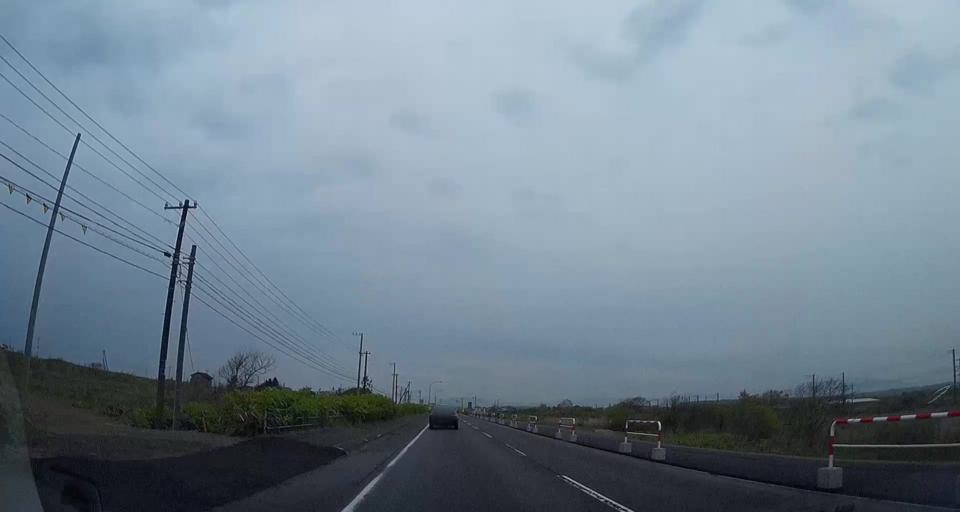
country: JP
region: Hokkaido
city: Shiraoi
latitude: 42.5812
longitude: 141.4268
